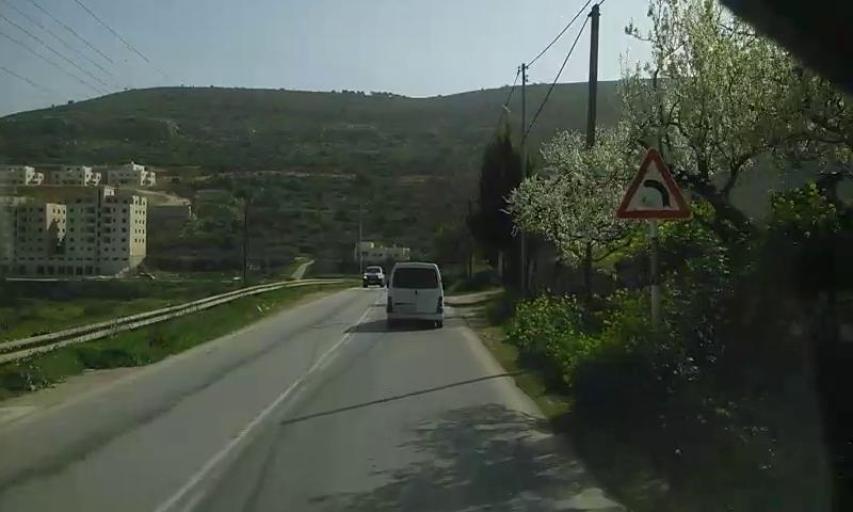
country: PS
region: West Bank
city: Dura al Qar`
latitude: 31.9711
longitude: 35.2326
